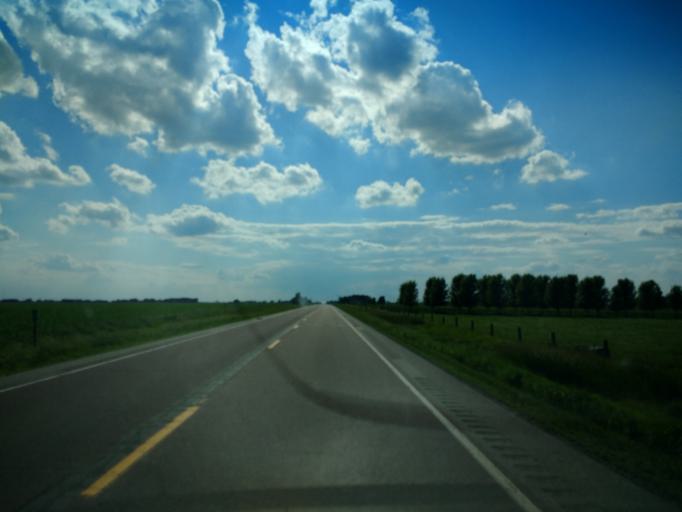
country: US
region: Iowa
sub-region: Clay County
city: Spencer
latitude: 43.1841
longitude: -95.2026
